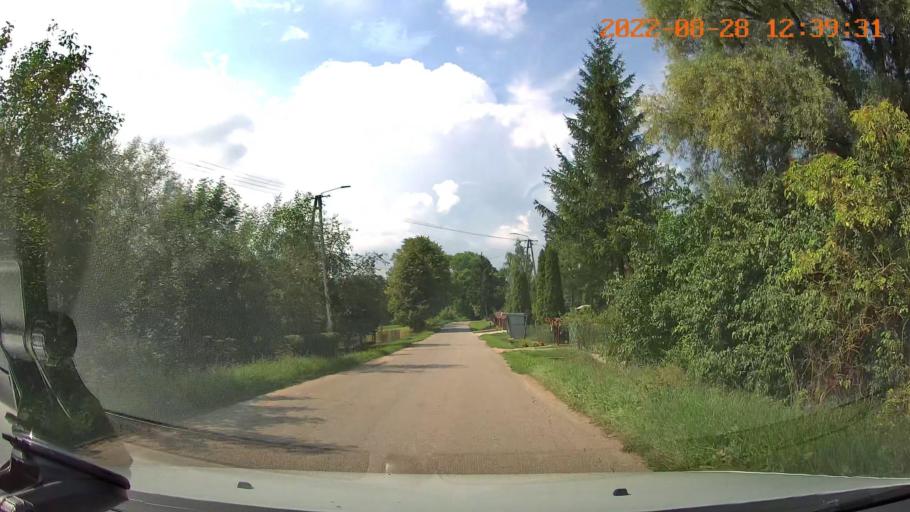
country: PL
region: Swietokrzyskie
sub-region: Powiat pinczowski
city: Dzialoszyce
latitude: 50.3728
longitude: 20.3737
